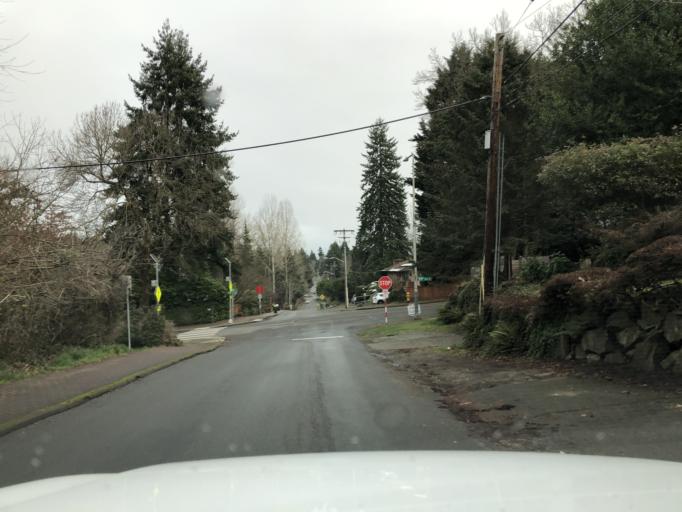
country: US
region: Washington
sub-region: King County
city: Lake Forest Park
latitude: 47.7048
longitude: -122.2915
